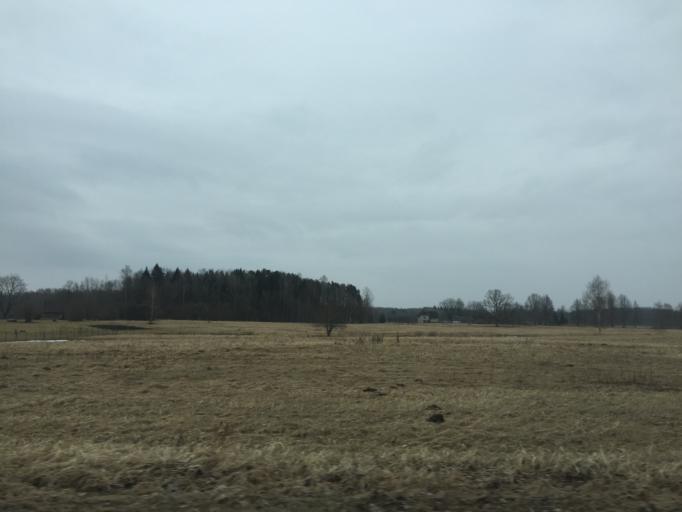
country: LV
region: Lielvarde
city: Lielvarde
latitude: 56.7495
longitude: 24.8358
